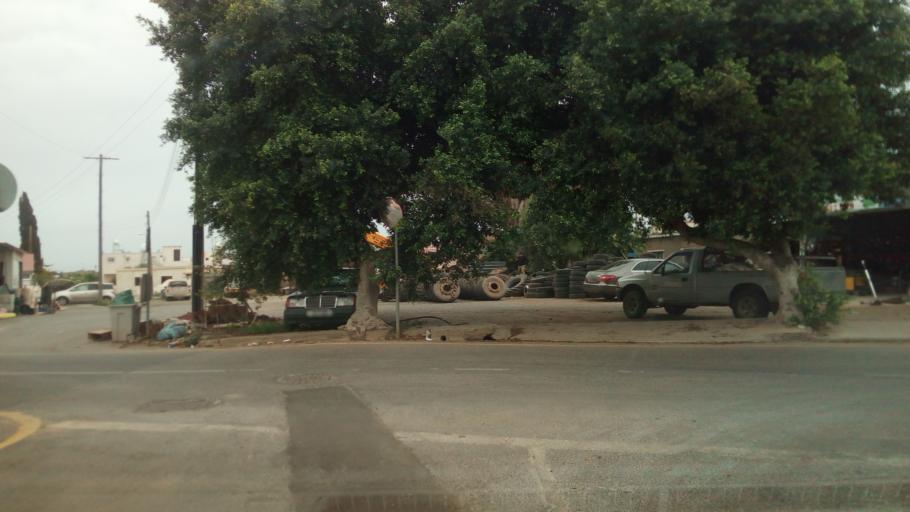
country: CY
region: Ammochostos
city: Liopetri
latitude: 34.9764
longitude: 33.8490
